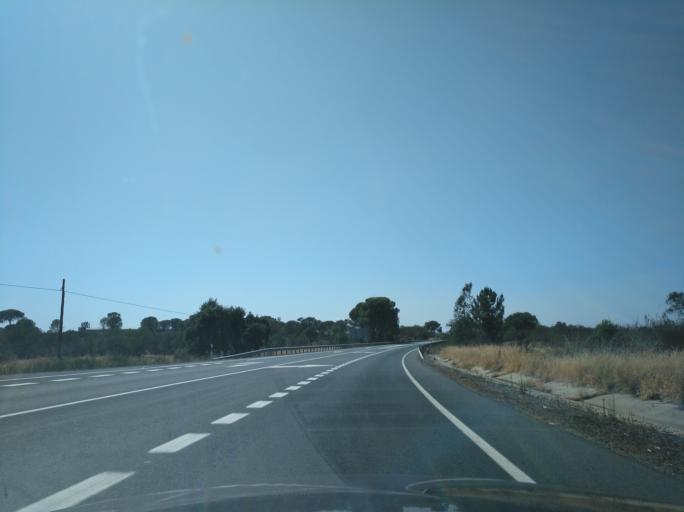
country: ES
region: Andalusia
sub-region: Provincia de Huelva
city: San Bartolome de la Torre
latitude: 37.4292
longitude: -7.0548
